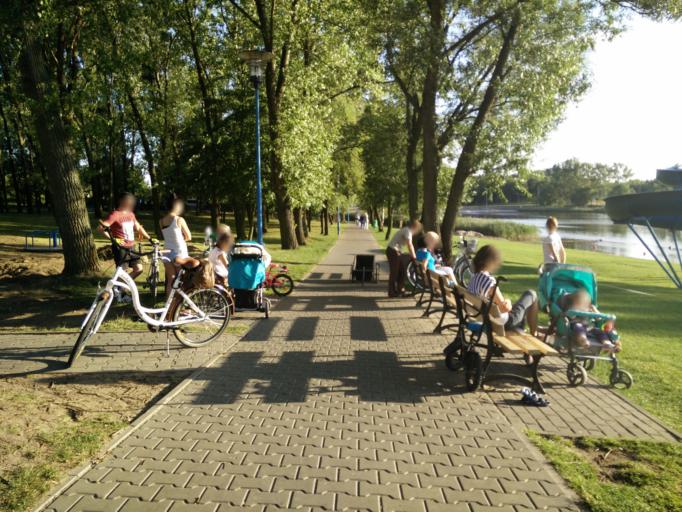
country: PL
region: Greater Poland Voivodeship
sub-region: Powiat sredzki
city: Sroda Wielkopolska
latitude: 52.2372
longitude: 17.2927
